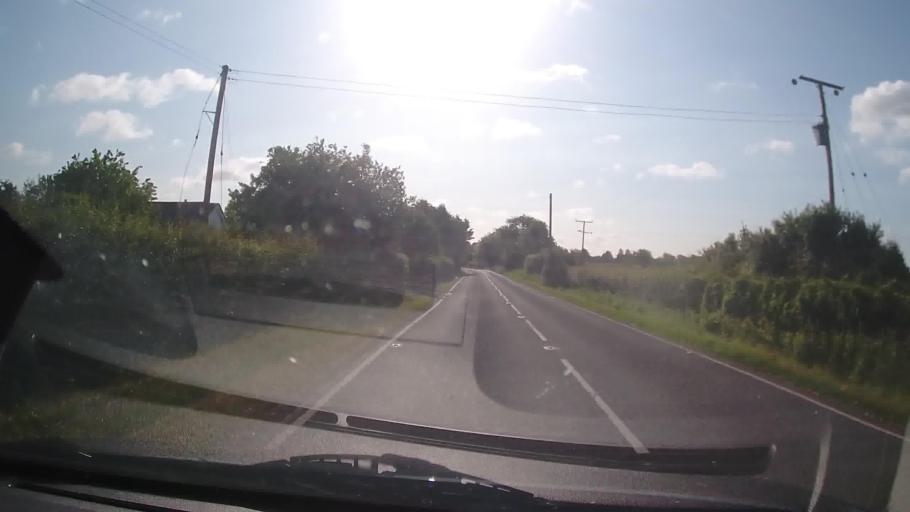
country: GB
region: England
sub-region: Shropshire
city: Shawbury
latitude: 52.7635
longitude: -2.6178
